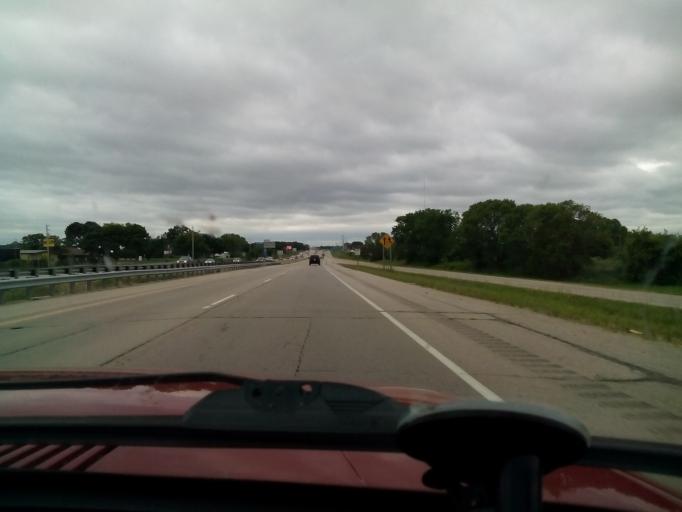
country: US
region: Wisconsin
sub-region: Dane County
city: Sun Prairie
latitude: 43.1752
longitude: -89.2508
